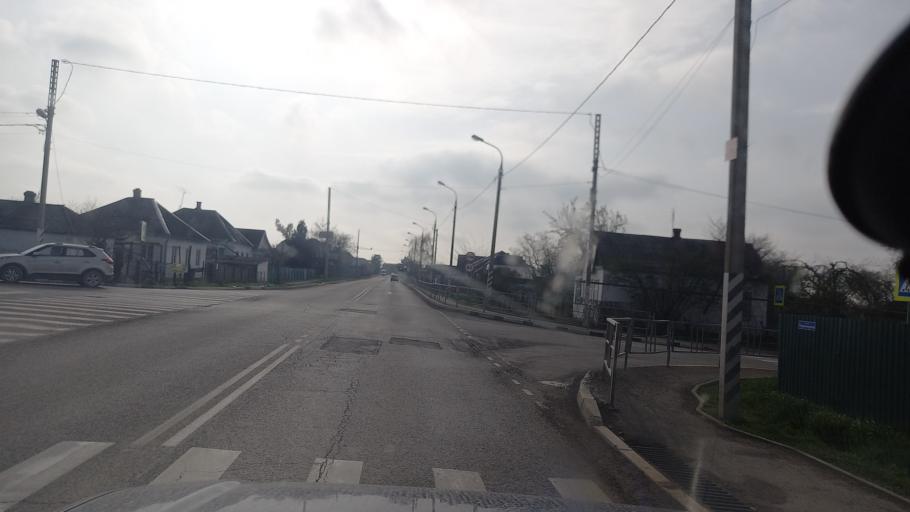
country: RU
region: Krasnodarskiy
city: Varenikovskaya
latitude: 45.1122
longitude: 37.6401
